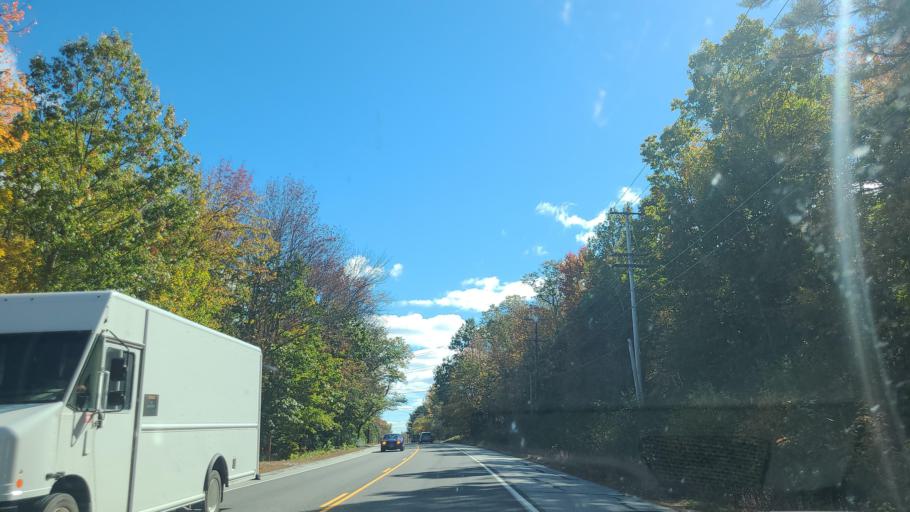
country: US
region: Maine
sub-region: Cumberland County
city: Bridgton
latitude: 43.9755
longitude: -70.6183
